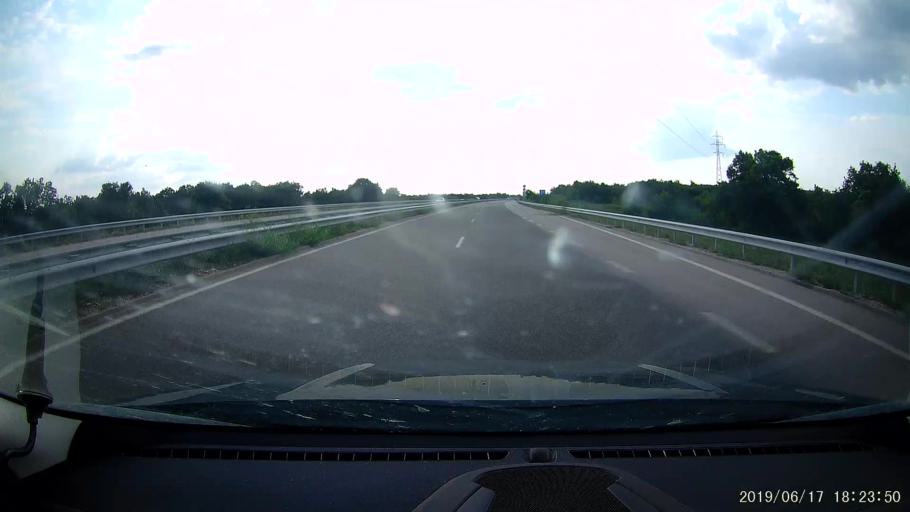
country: BG
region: Khaskovo
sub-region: Obshtina Dimitrovgrad
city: Dimitrovgrad
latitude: 41.9780
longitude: 25.7088
